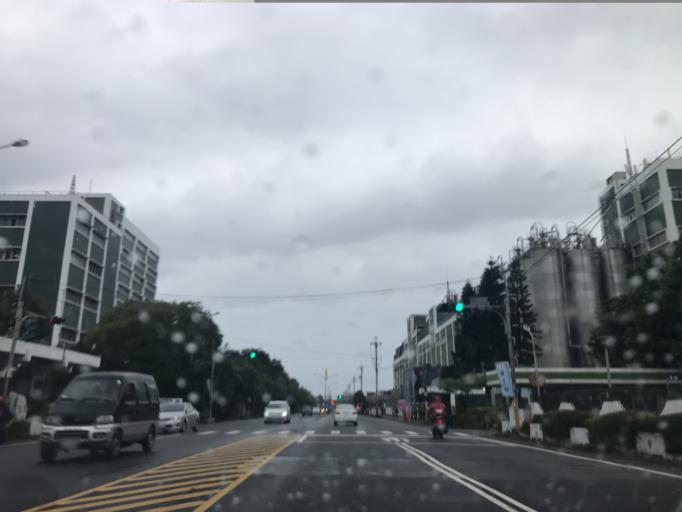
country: TW
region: Taiwan
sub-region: Hsinchu
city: Zhubei
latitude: 24.8253
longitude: 121.0579
